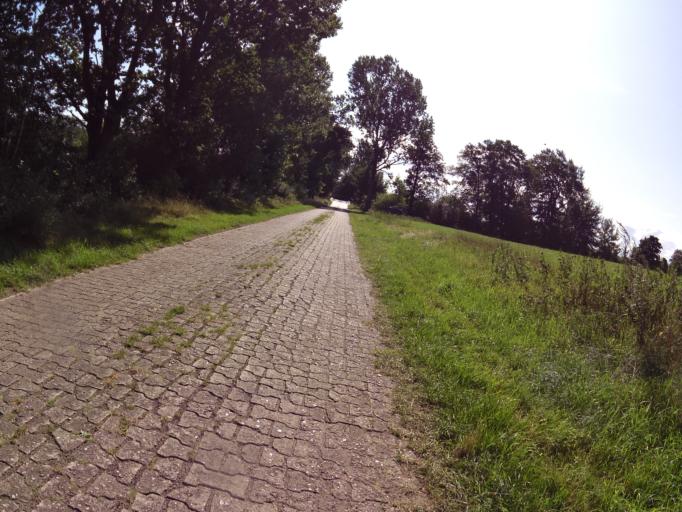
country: DE
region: Lower Saxony
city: Sandbostel
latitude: 53.3874
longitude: 9.1273
